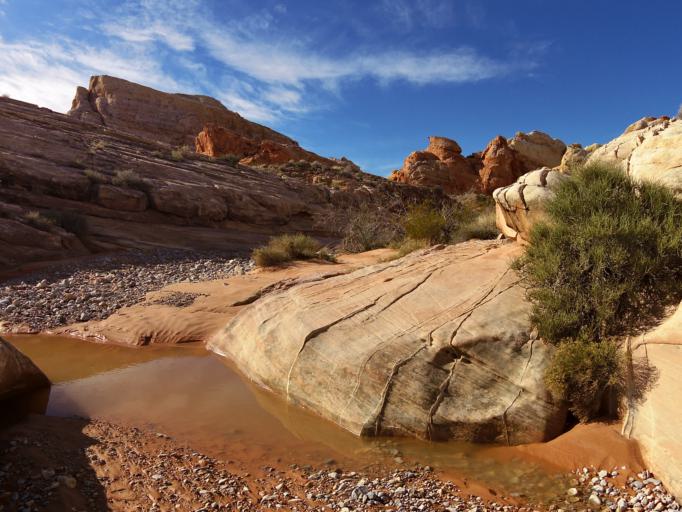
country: US
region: Nevada
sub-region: Clark County
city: Moapa Valley
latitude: 36.4804
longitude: -114.5291
